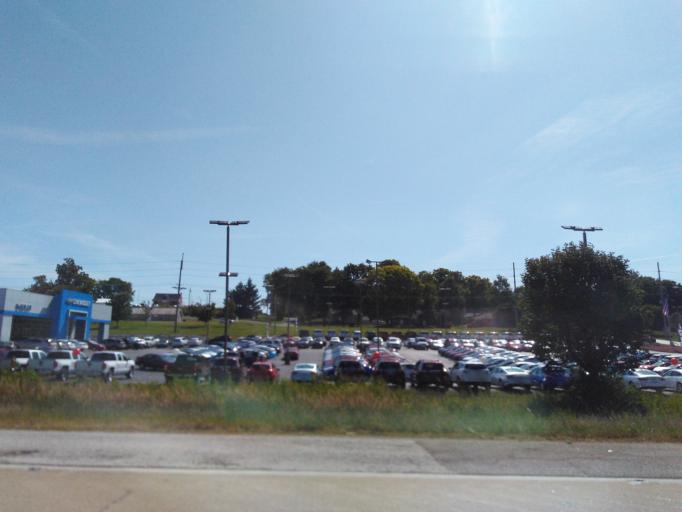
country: US
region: Illinois
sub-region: Saint Clair County
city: Dupo
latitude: 38.4805
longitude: -90.2224
